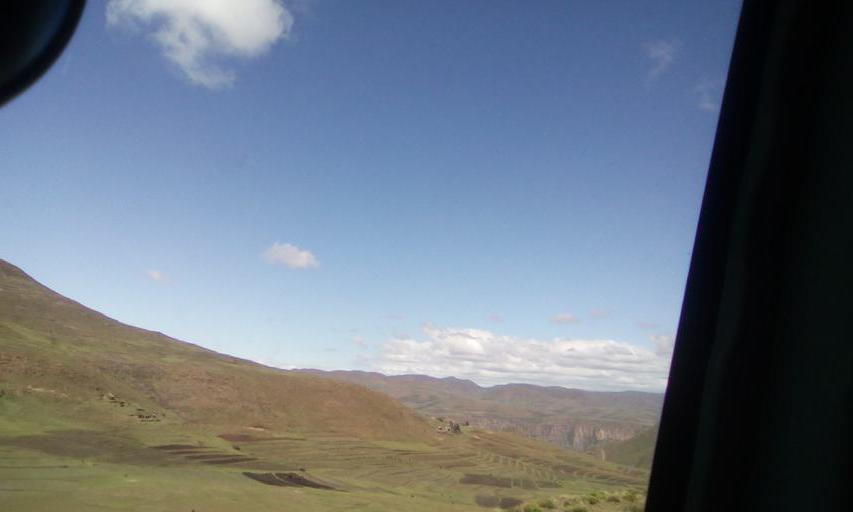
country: LS
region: Maseru
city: Nako
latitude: -29.8878
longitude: 28.1066
